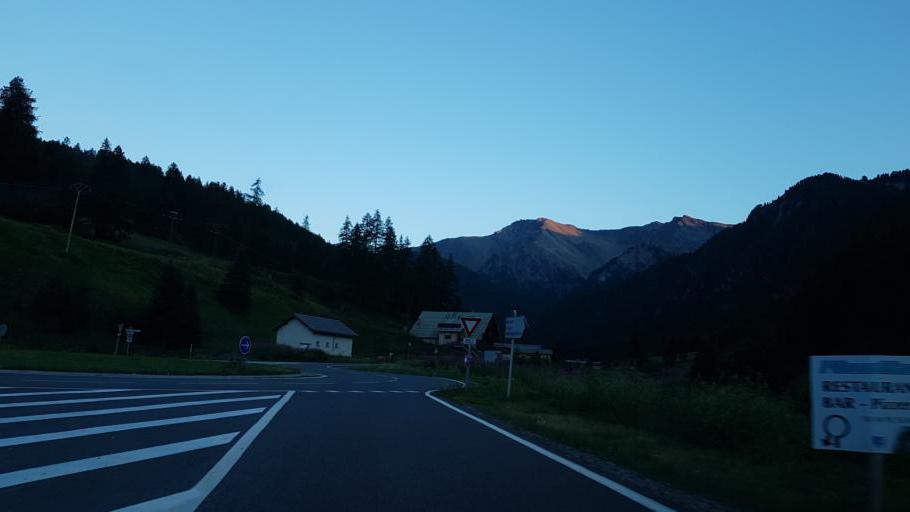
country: FR
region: Provence-Alpes-Cote d'Azur
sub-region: Departement des Hautes-Alpes
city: Guillestre
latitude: 44.7186
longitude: 6.8474
